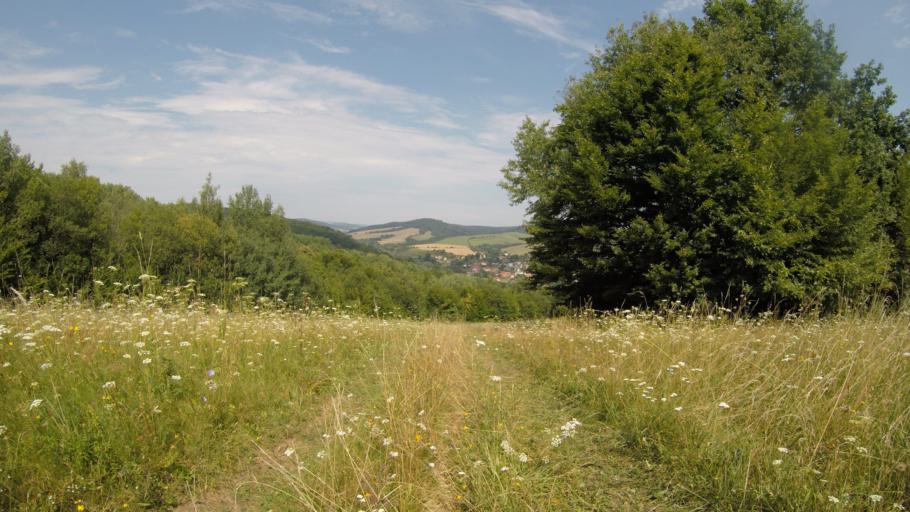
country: SK
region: Presovsky
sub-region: Okres Presov
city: Presov
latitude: 48.9401
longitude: 21.1671
